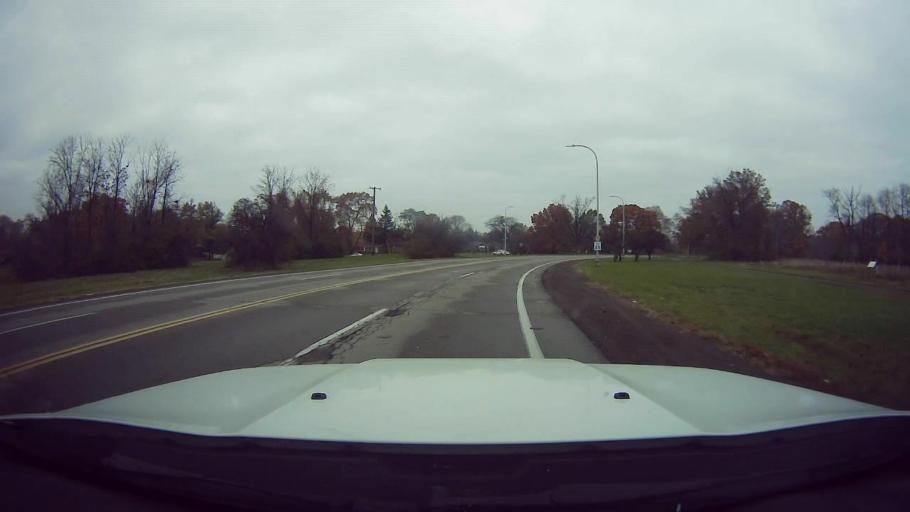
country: US
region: Michigan
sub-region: Wayne County
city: Dearborn Heights
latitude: 42.3587
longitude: -83.2640
